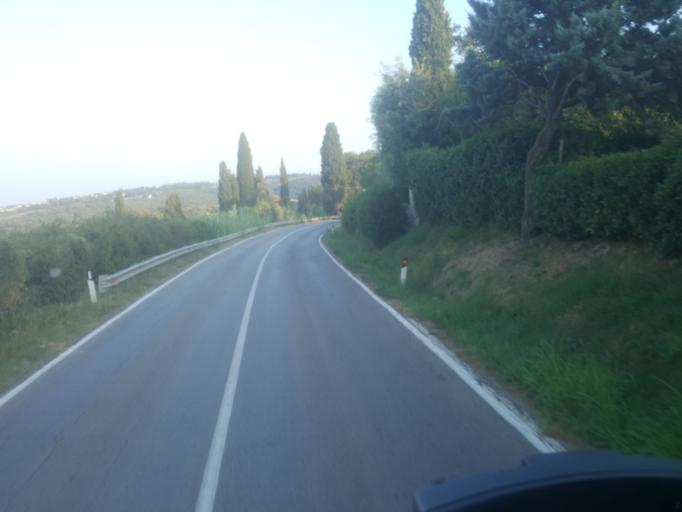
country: IT
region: Tuscany
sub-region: Province of Florence
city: Montaione
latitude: 43.5459
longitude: 10.9256
